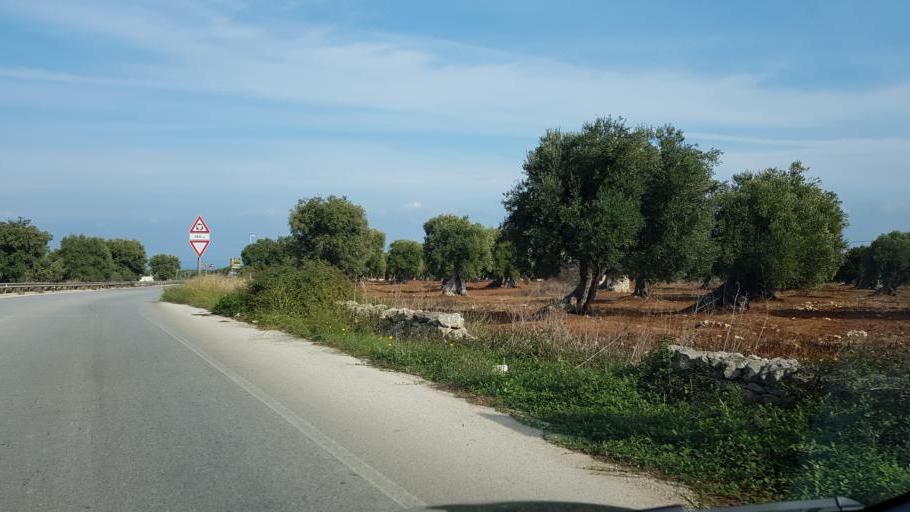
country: IT
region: Apulia
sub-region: Provincia di Brindisi
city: Ostuni
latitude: 40.7558
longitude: 17.5833
